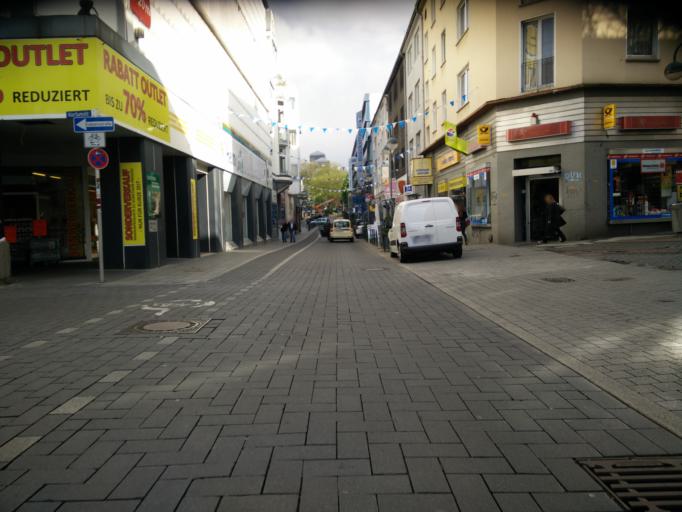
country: DE
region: North Rhine-Westphalia
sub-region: Regierungsbezirk Arnsberg
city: Bochum
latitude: 51.4838
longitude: 7.2175
